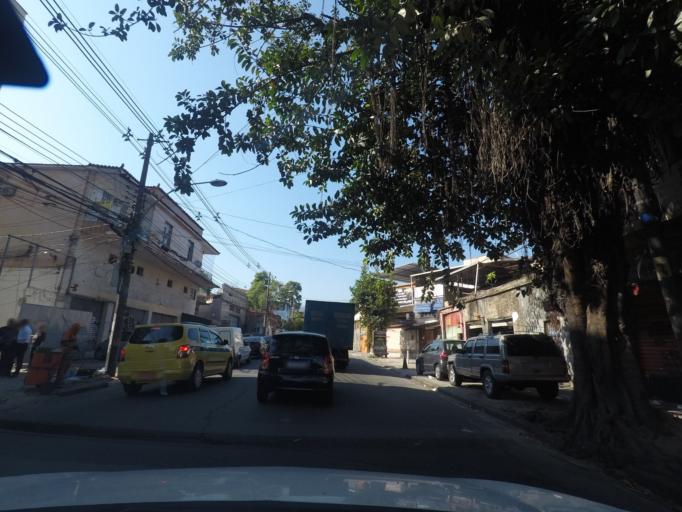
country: BR
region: Rio de Janeiro
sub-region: Rio De Janeiro
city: Rio de Janeiro
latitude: -22.8979
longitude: -43.2404
